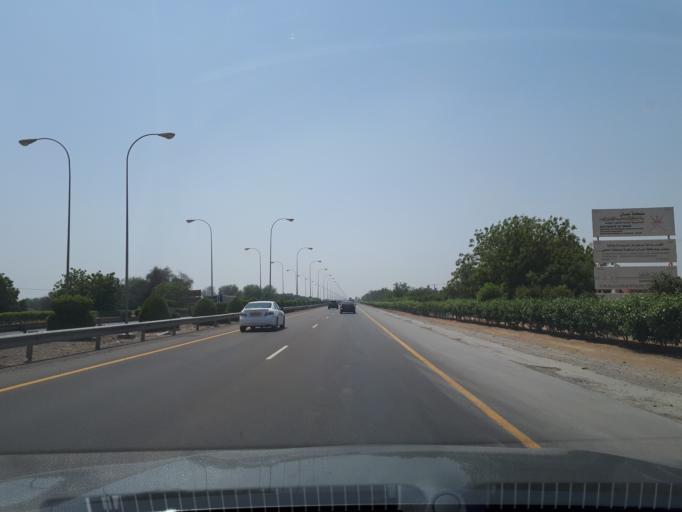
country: OM
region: Al Batinah
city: Al Sohar
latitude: 24.3995
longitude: 56.6657
